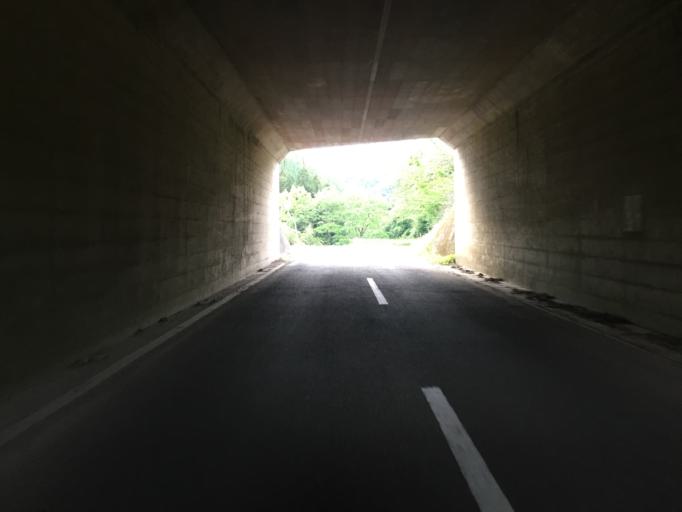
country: JP
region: Fukushima
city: Yanagawamachi-saiwaicho
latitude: 37.8998
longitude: 140.6620
